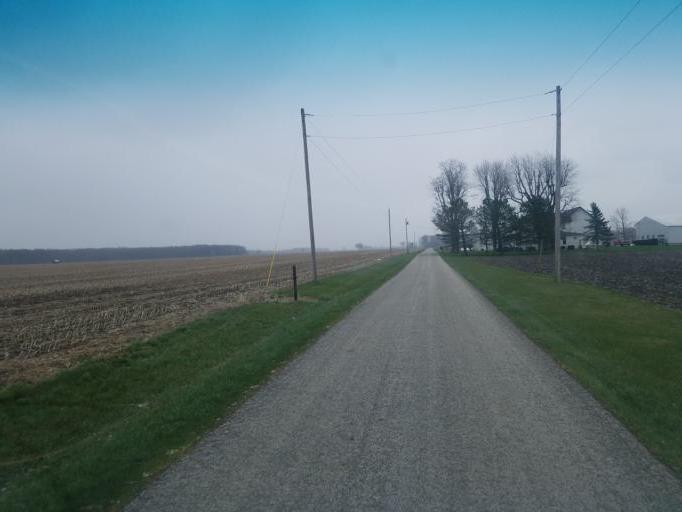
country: US
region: Ohio
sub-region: Marion County
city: Prospect
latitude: 40.4163
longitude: -83.1243
